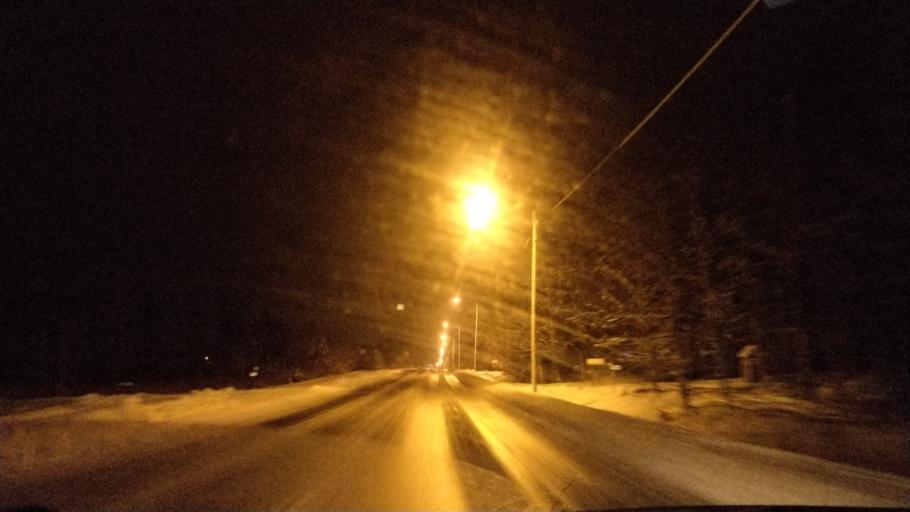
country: FI
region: Lapland
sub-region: Rovaniemi
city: Rovaniemi
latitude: 66.3976
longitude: 25.3861
